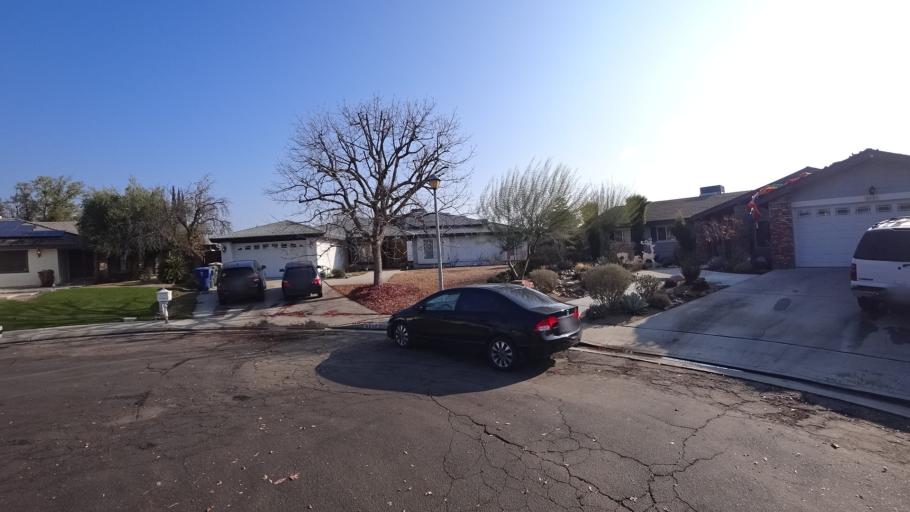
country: US
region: California
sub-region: Kern County
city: Greenacres
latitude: 35.3374
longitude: -119.0808
